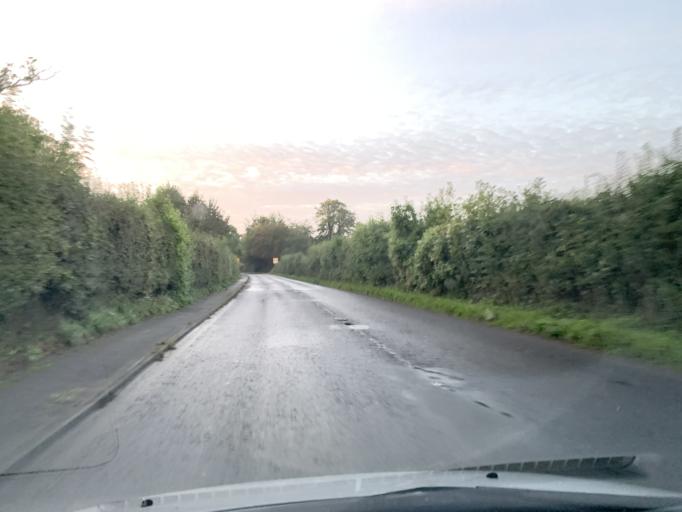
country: GB
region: England
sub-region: Wiltshire
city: Alderbury
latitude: 51.0471
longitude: -1.7437
